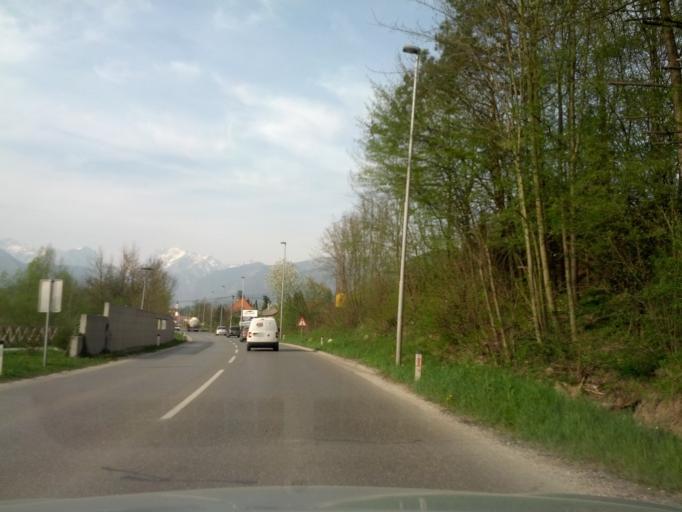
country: SI
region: Kamnik
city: Kamnik
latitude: 46.2114
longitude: 14.6086
